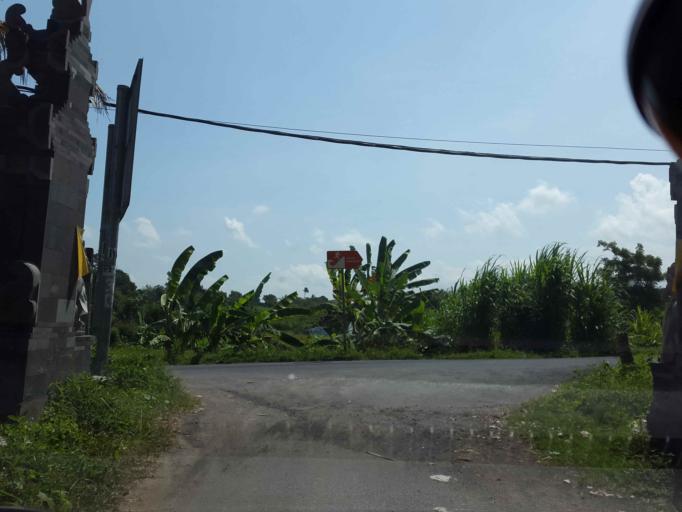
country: ID
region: Bali
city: Klungkung
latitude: -8.5675
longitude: 115.3737
